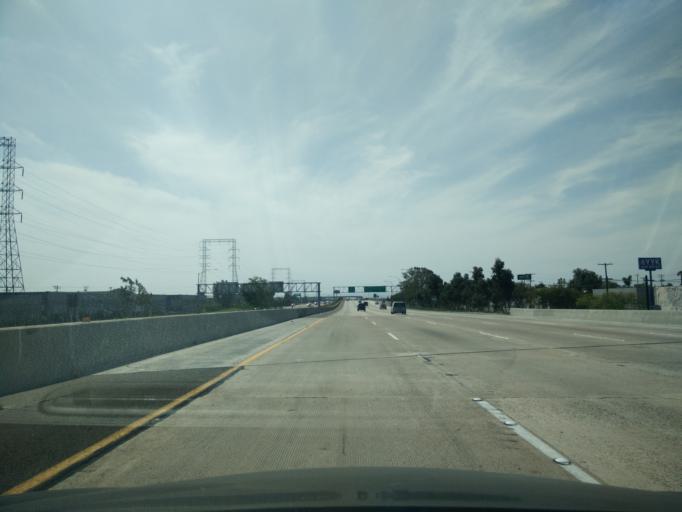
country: US
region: California
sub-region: San Diego County
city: National City
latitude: 32.6650
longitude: -117.1101
